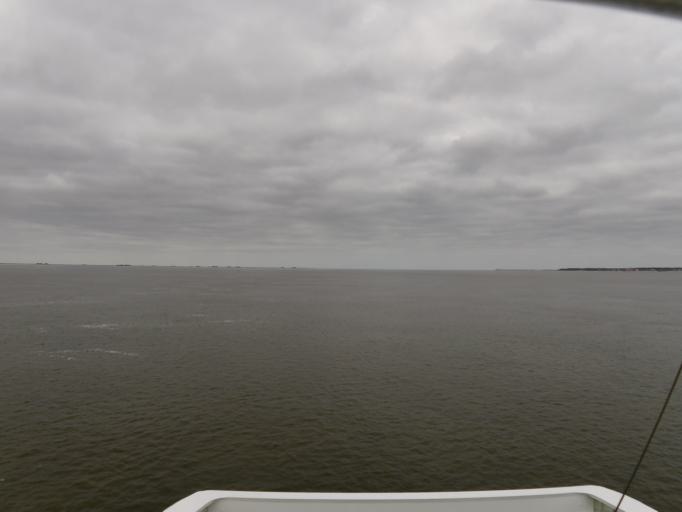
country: DE
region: Schleswig-Holstein
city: Wyk auf Fohr
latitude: 54.6944
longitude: 8.6292
